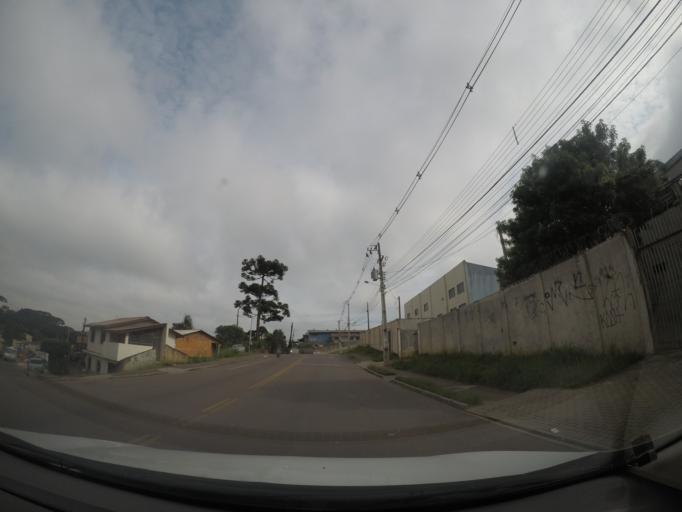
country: BR
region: Parana
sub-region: Colombo
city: Colombo
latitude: -25.3455
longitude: -49.2219
